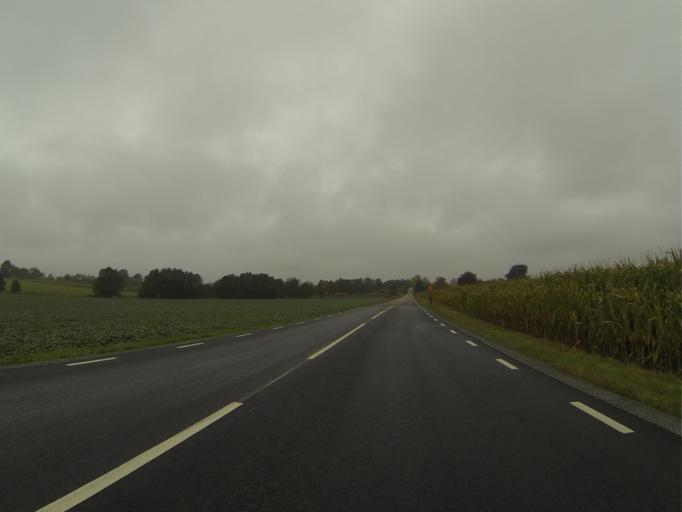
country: SE
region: Skane
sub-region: Tomelilla Kommun
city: Tomelilla
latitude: 55.5734
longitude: 13.9286
